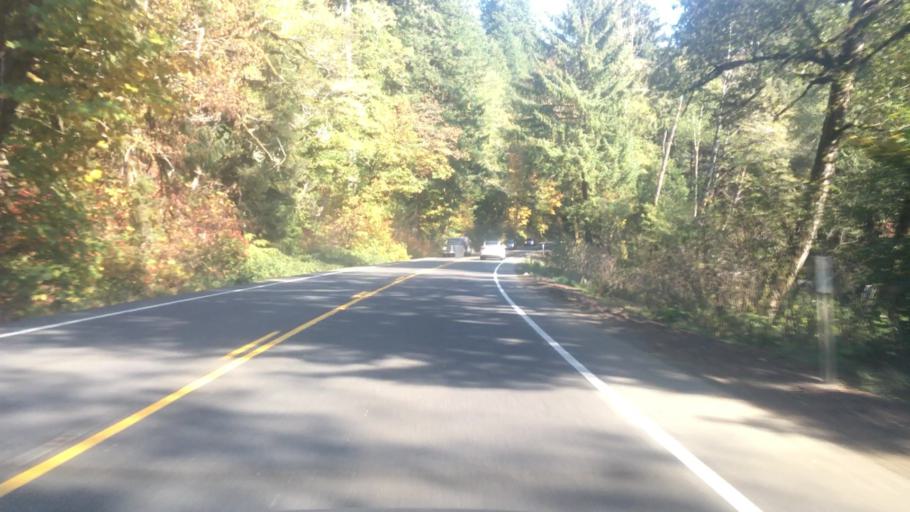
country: US
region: Oregon
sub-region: Lincoln County
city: Rose Lodge
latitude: 45.0521
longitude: -123.7777
